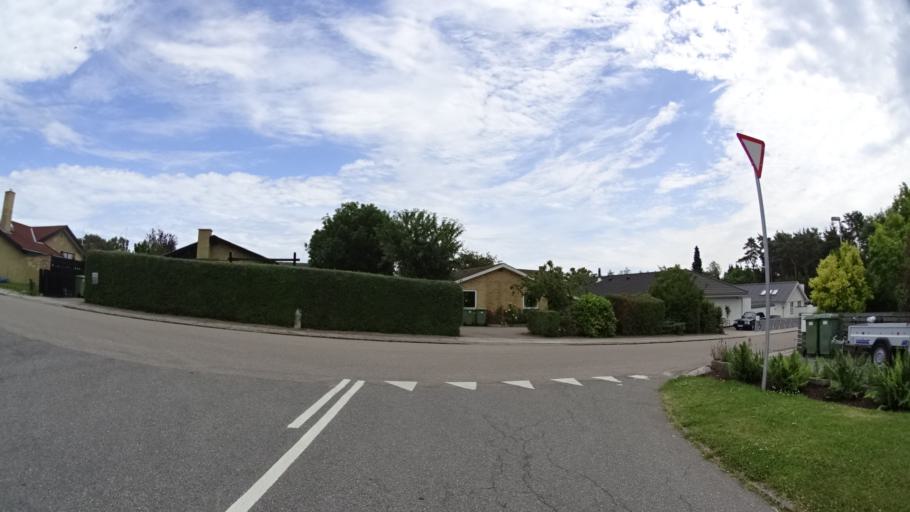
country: DK
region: Central Jutland
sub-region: Arhus Kommune
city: Stavtrup
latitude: 56.1272
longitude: 10.1443
